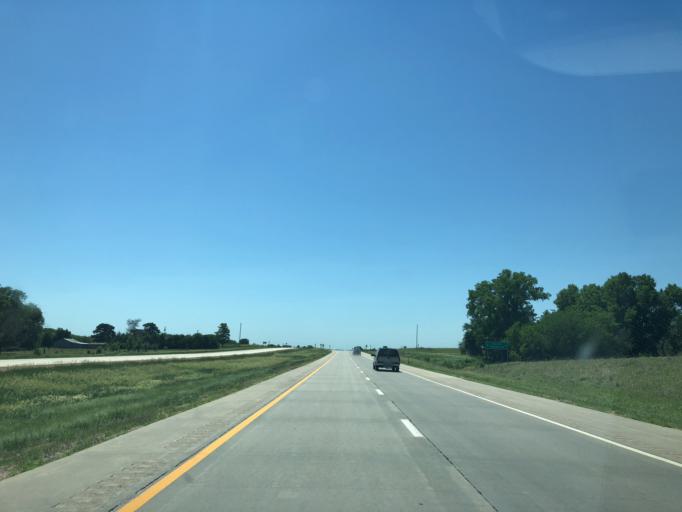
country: US
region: Kansas
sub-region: Cloud County
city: Concordia
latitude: 39.6567
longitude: -97.6605
